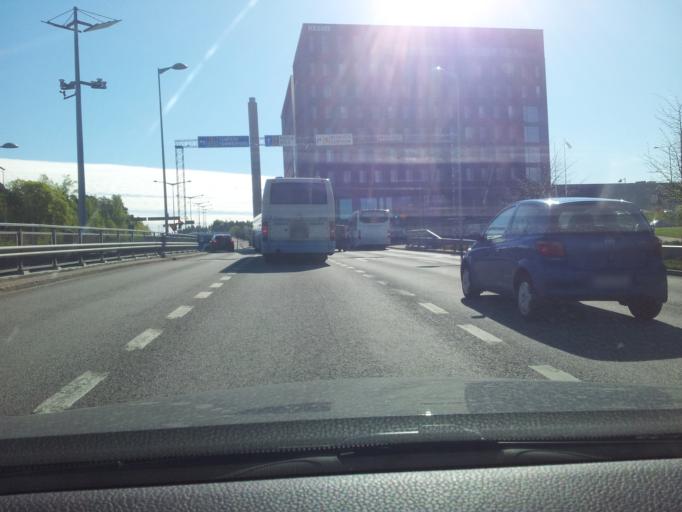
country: FI
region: Uusimaa
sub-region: Helsinki
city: Helsinki
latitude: 60.2080
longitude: 24.8978
